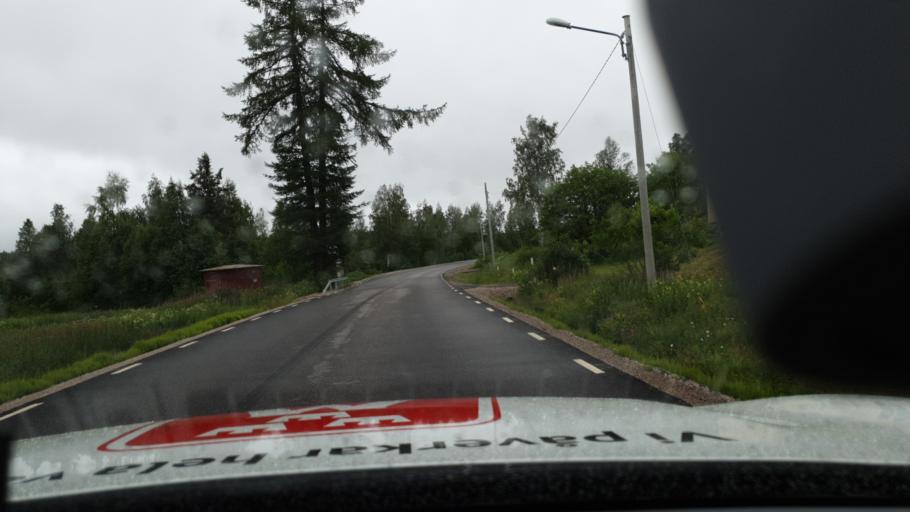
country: SE
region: Norrbotten
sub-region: Overtornea Kommun
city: OEvertornea
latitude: 66.4821
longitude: 23.4588
